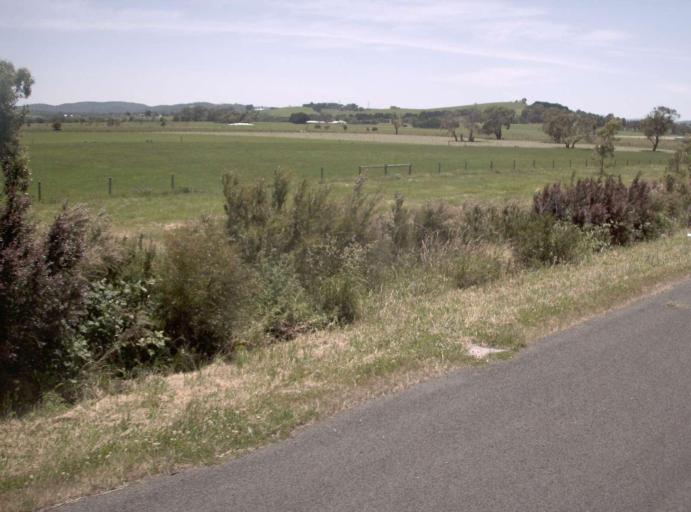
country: AU
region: Victoria
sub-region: Cardinia
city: Pakenham South
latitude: -38.0755
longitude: 145.5354
